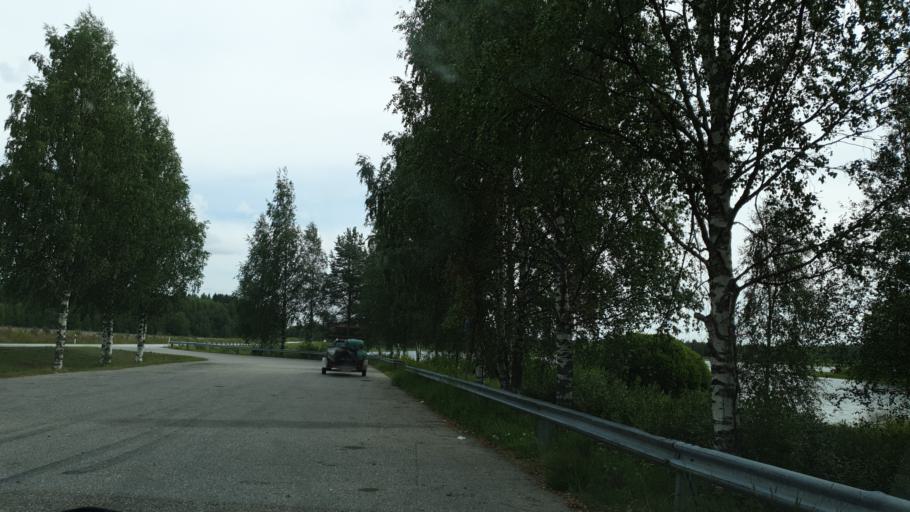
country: FI
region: North Karelia
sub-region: Pielisen Karjala
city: Valtimo
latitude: 63.7025
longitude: 28.7674
